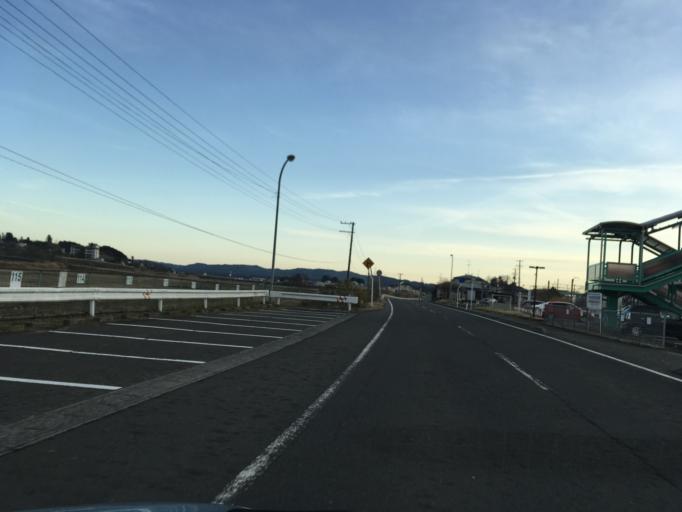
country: JP
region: Miyagi
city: Kogota
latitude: 38.6560
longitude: 141.0742
